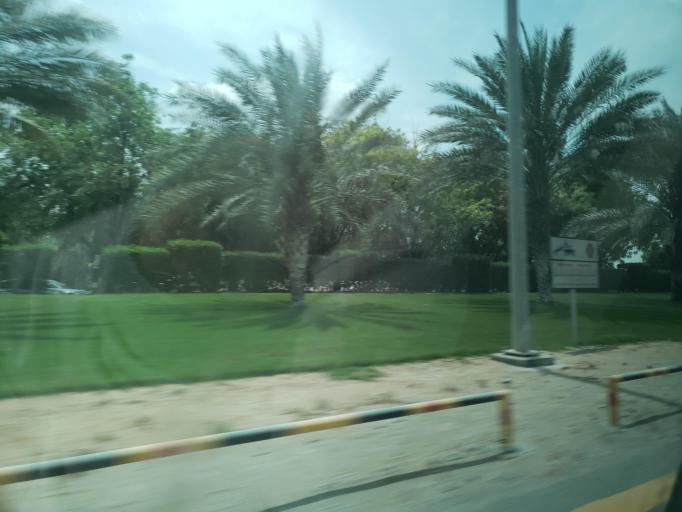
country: AE
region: Ash Shariqah
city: Sharjah
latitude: 25.3208
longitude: 55.5169
